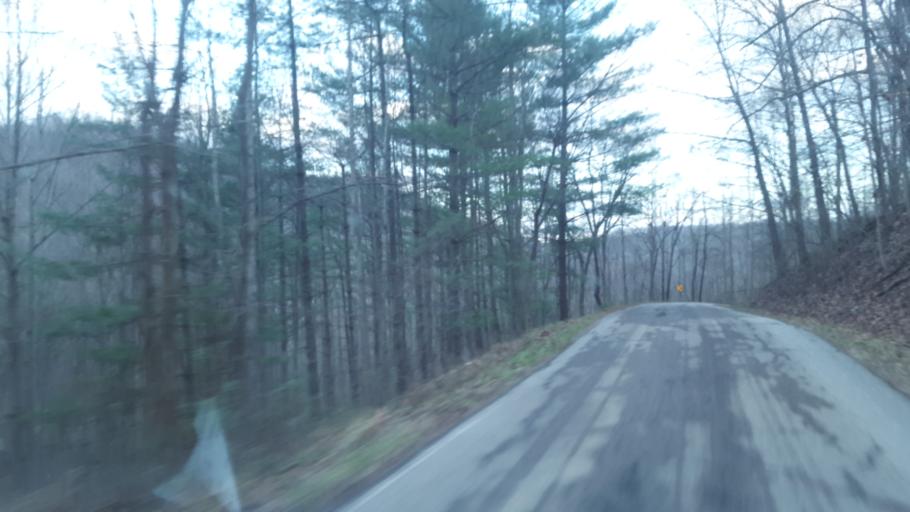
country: US
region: Ohio
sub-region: Adams County
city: Manchester
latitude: 38.5160
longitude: -83.5091
